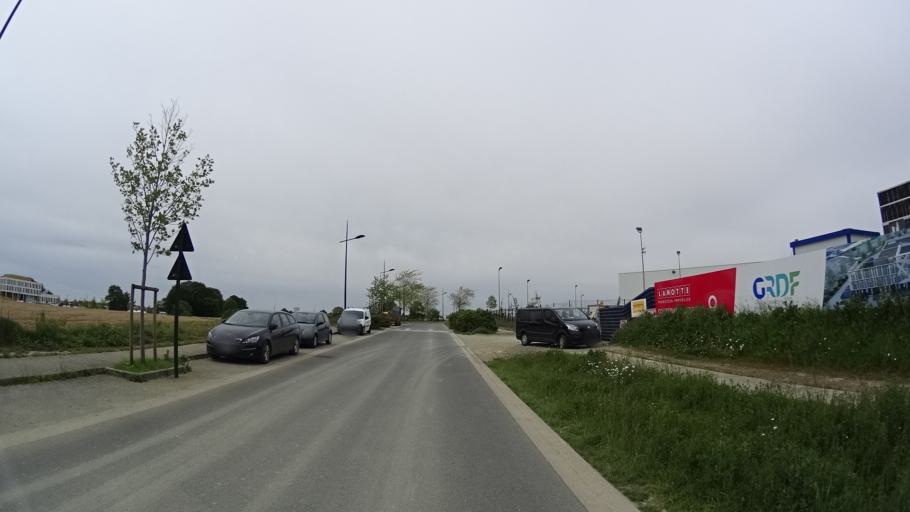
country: FR
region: Brittany
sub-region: Departement d'Ille-et-Vilaine
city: Pace
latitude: 48.1421
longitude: -1.7603
